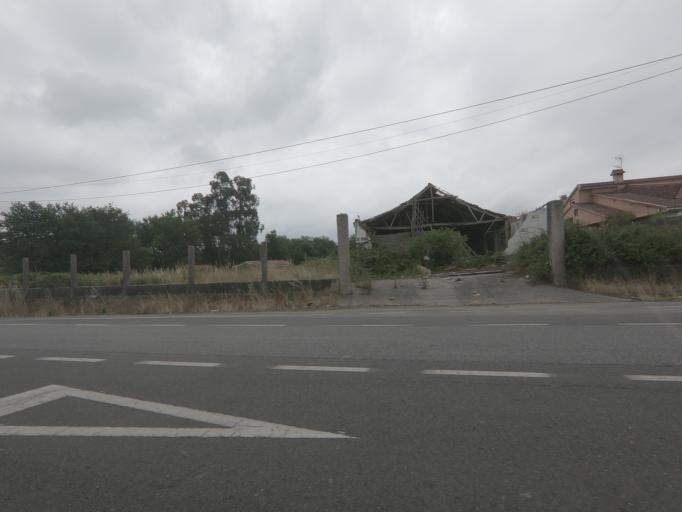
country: ES
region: Galicia
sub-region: Provincia de Pontevedra
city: Tomino
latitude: 41.9797
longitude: -8.7333
